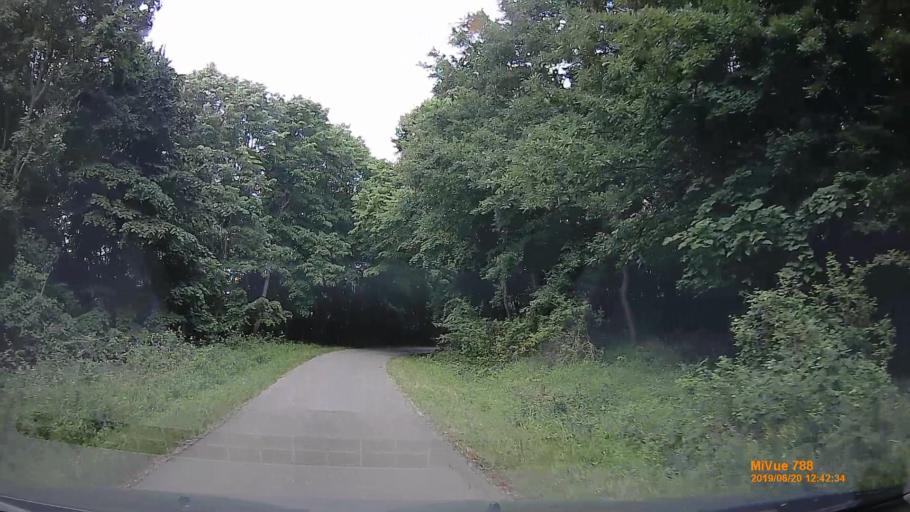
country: HU
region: Baranya
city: Hosszuheteny
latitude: 46.1979
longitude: 18.3590
